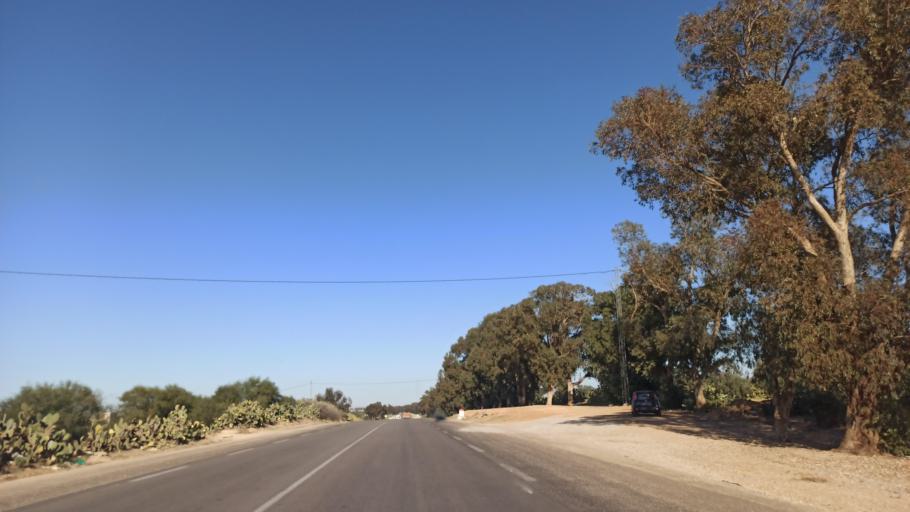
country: TN
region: Sidi Bu Zayd
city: Jilma
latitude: 35.1656
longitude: 9.3687
